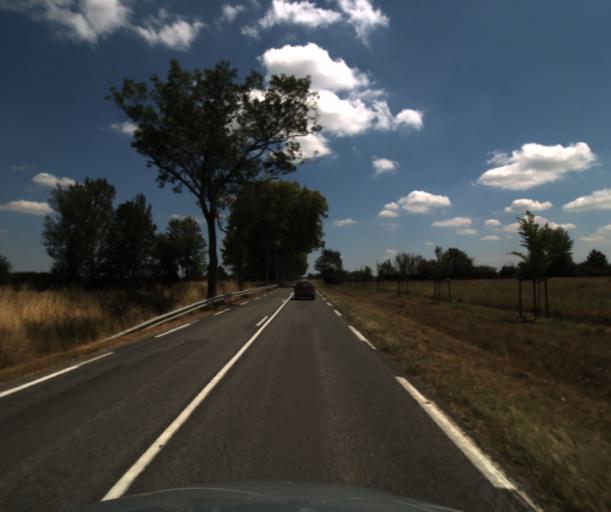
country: FR
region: Midi-Pyrenees
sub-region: Departement de la Haute-Garonne
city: Labastidette
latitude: 43.4684
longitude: 1.2291
